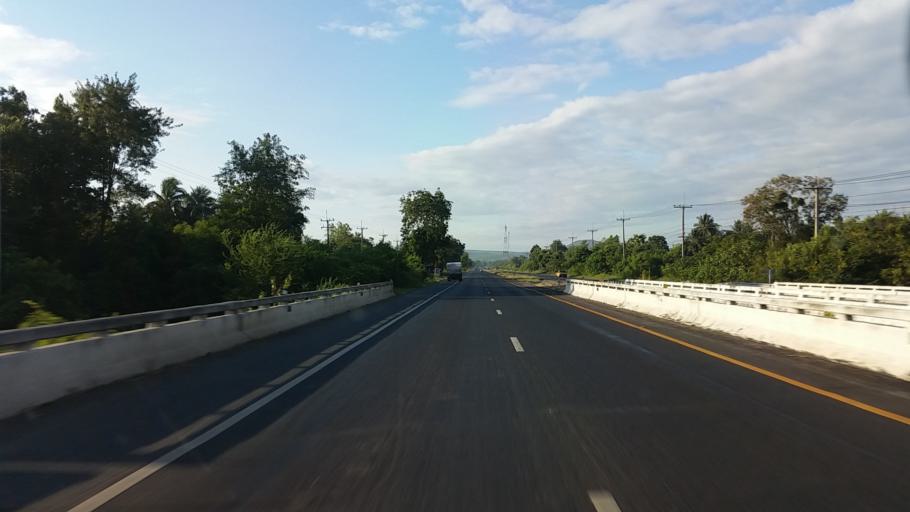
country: TH
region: Lop Buri
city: Phatthana Nikhom
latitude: 15.0080
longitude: 100.9415
